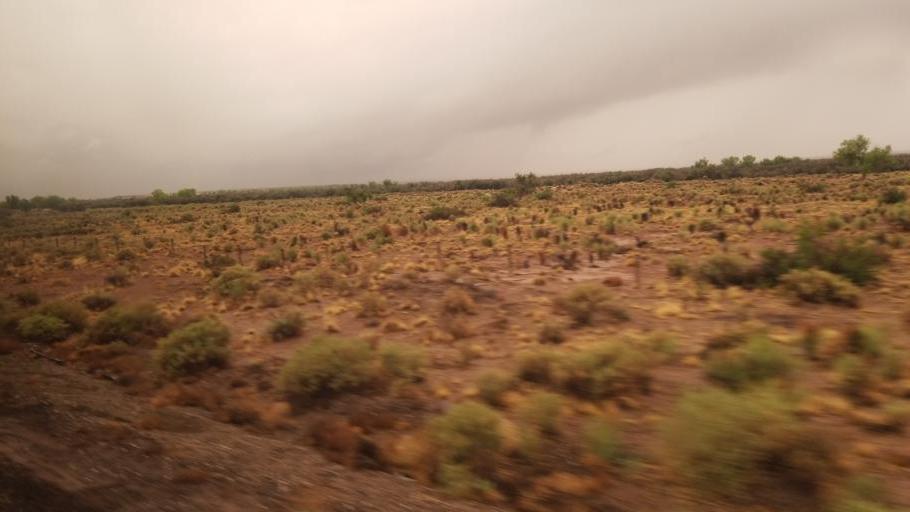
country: US
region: Arizona
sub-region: Navajo County
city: Joseph City
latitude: 34.9672
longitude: -110.4354
